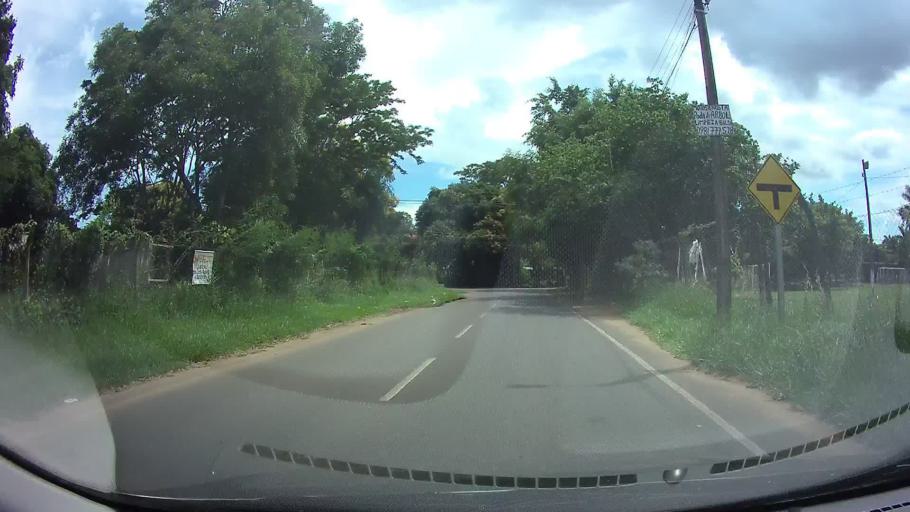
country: PY
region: Central
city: Fernando de la Mora
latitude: -25.3209
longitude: -57.5304
